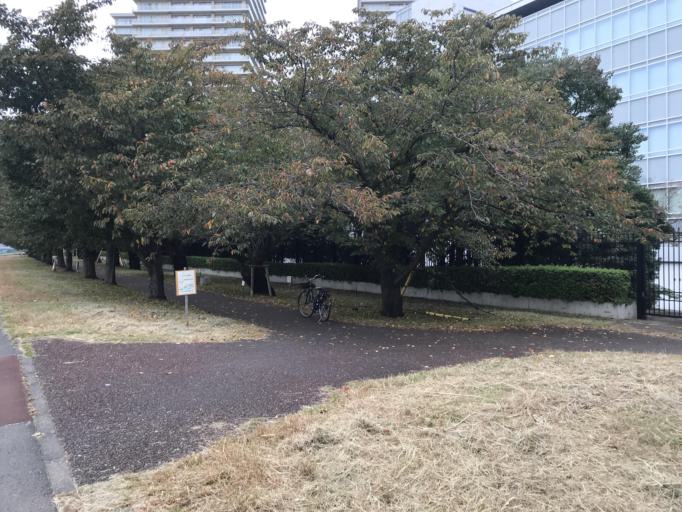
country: JP
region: Kanagawa
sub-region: Kawasaki-shi
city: Kawasaki
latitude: 35.5664
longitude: 139.6796
